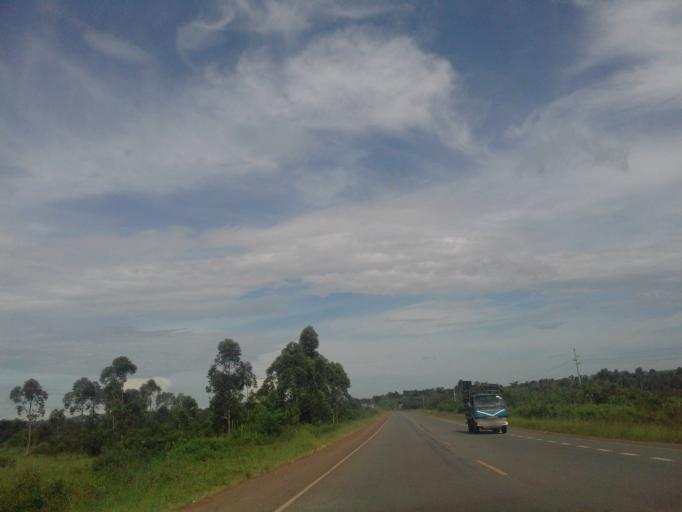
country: UG
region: Central Region
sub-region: Lwengo District
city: Lwengo
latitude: -0.3719
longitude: 31.5248
